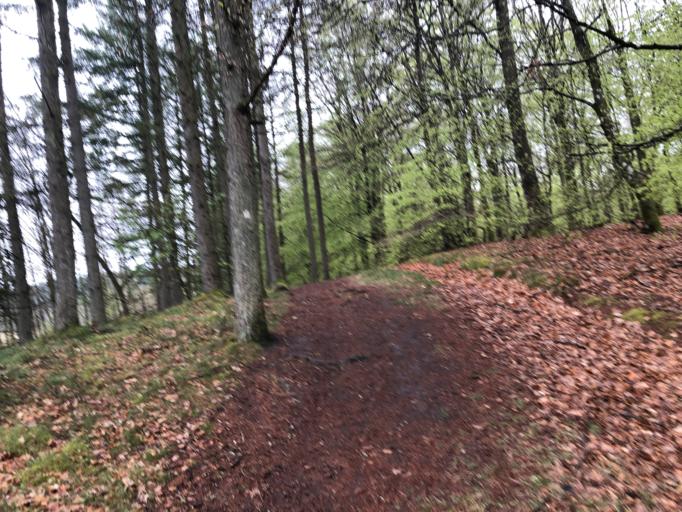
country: DK
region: Central Jutland
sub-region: Lemvig Kommune
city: Lemvig
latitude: 56.4822
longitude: 8.3556
